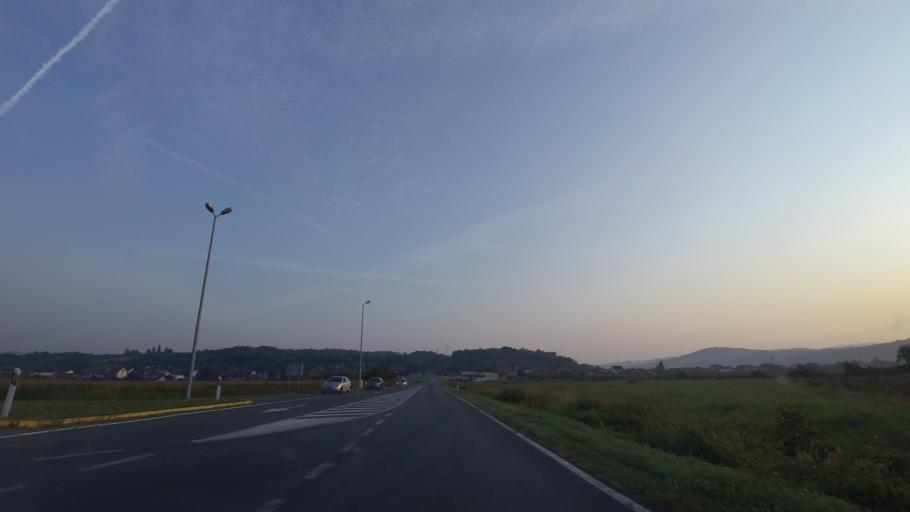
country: HR
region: Brodsko-Posavska
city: Nova Gradiska
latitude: 45.2530
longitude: 17.4093
